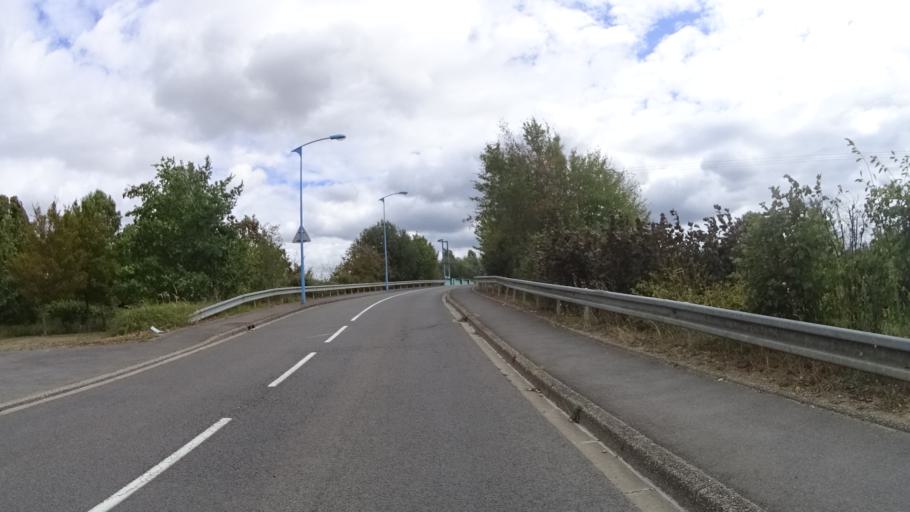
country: FR
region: Picardie
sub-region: Departement de l'Aisne
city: Tergnier
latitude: 49.6522
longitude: 3.3152
